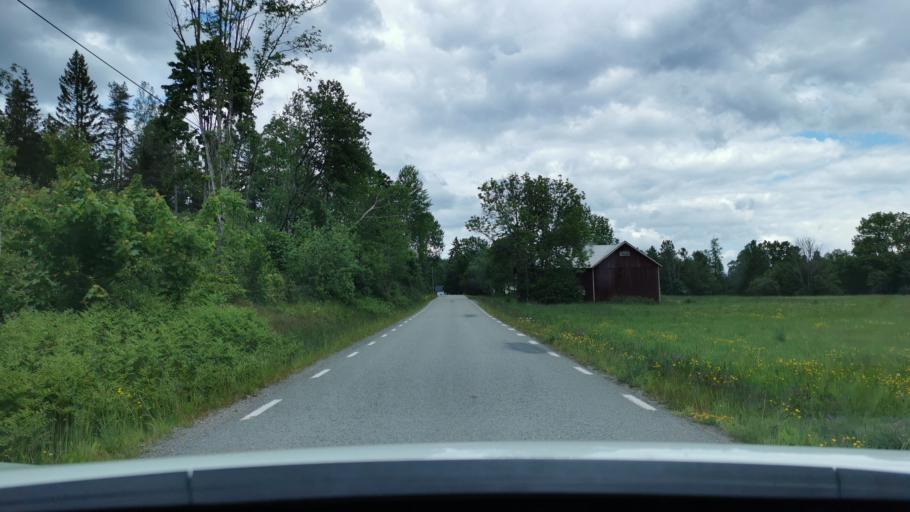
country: SE
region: Vaestra Goetaland
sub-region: Bengtsfors Kommun
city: Dals Langed
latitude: 58.7980
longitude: 12.3286
